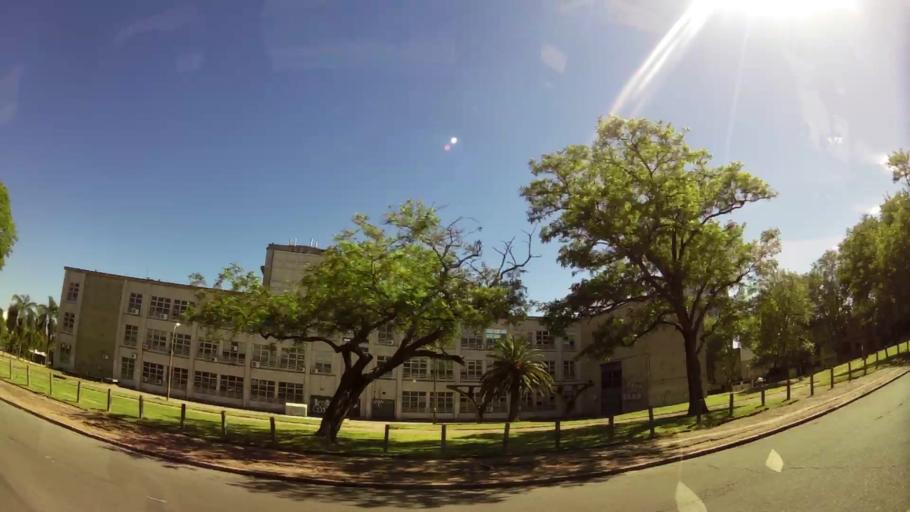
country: UY
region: Montevideo
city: Montevideo
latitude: -34.9197
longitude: -56.1665
